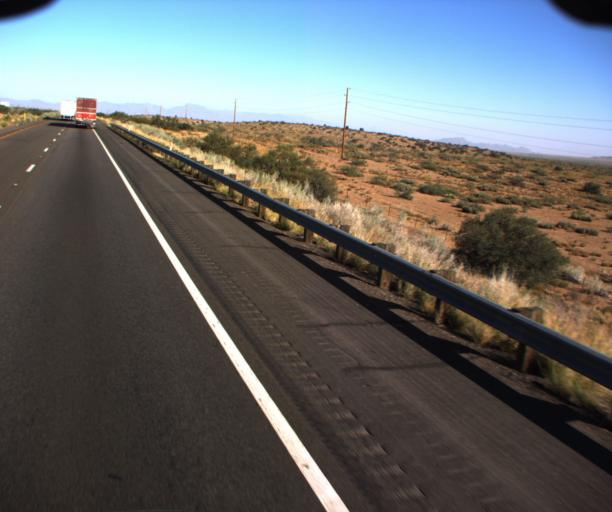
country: US
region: Arizona
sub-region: Mohave County
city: New Kingman-Butler
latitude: 35.1839
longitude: -113.8058
